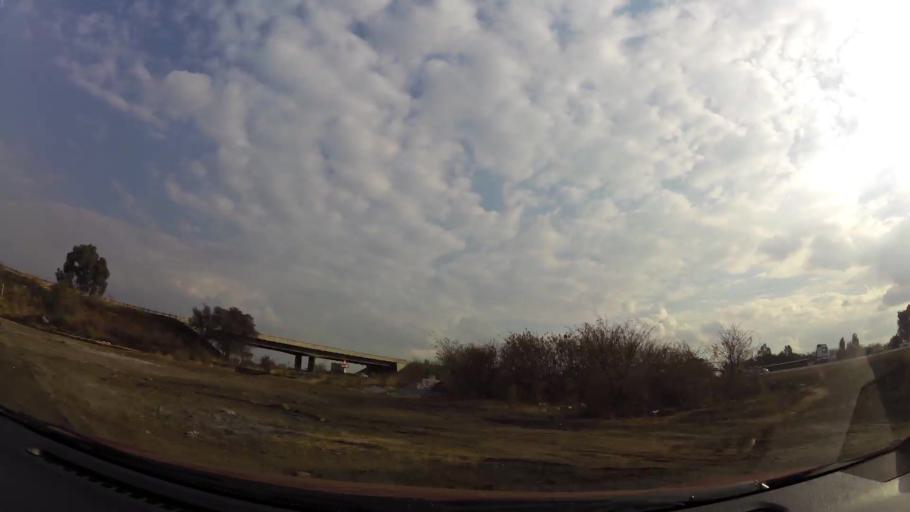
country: ZA
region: Gauteng
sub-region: Sedibeng District Municipality
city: Vereeniging
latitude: -26.6844
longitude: 27.9057
